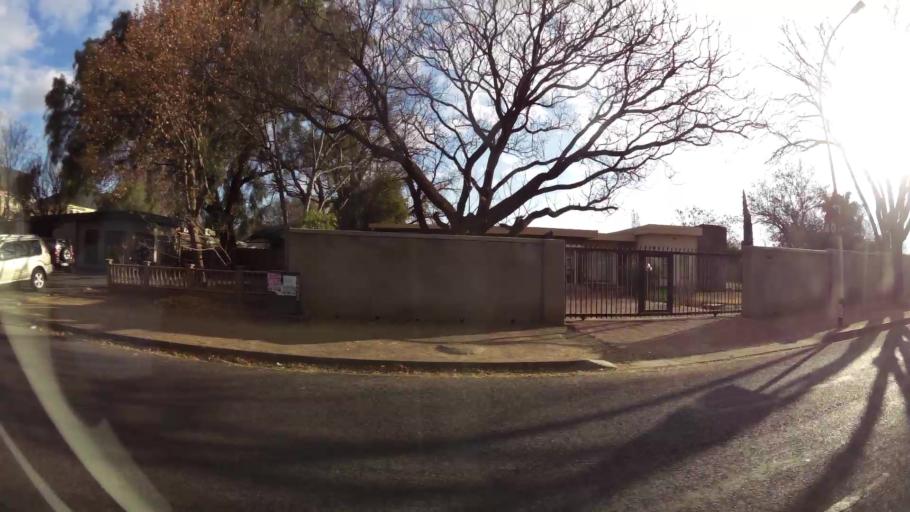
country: ZA
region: Orange Free State
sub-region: Mangaung Metropolitan Municipality
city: Bloemfontein
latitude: -29.1044
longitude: 26.1991
